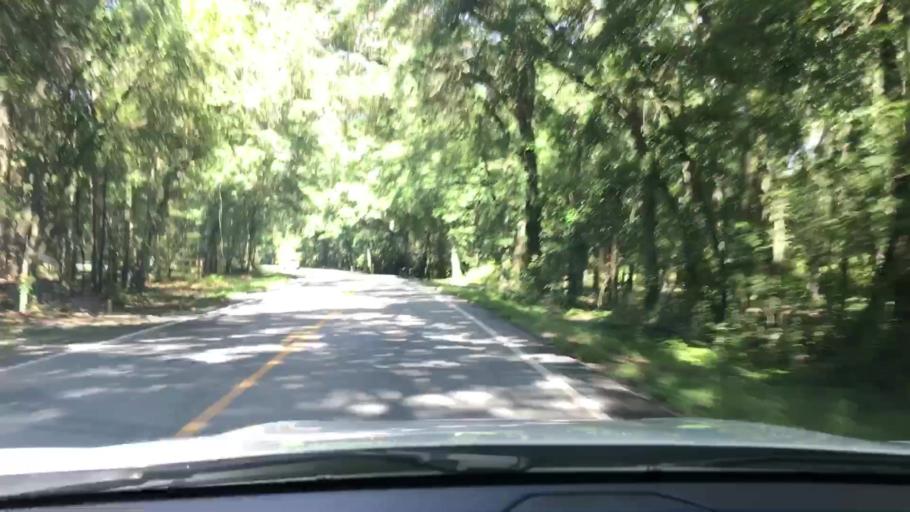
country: US
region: South Carolina
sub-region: Berkeley County
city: Ladson
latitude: 32.8877
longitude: -80.1169
